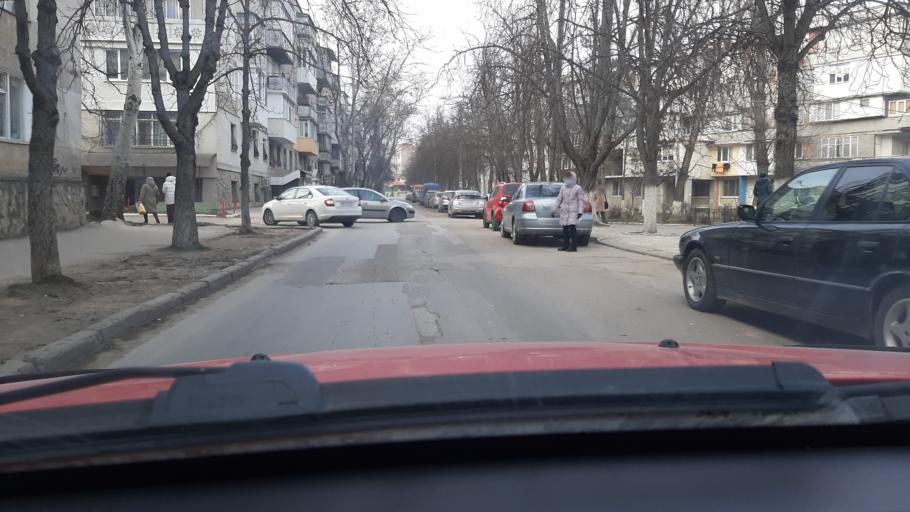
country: MD
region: Chisinau
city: Chisinau
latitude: 47.0306
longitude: 28.7935
